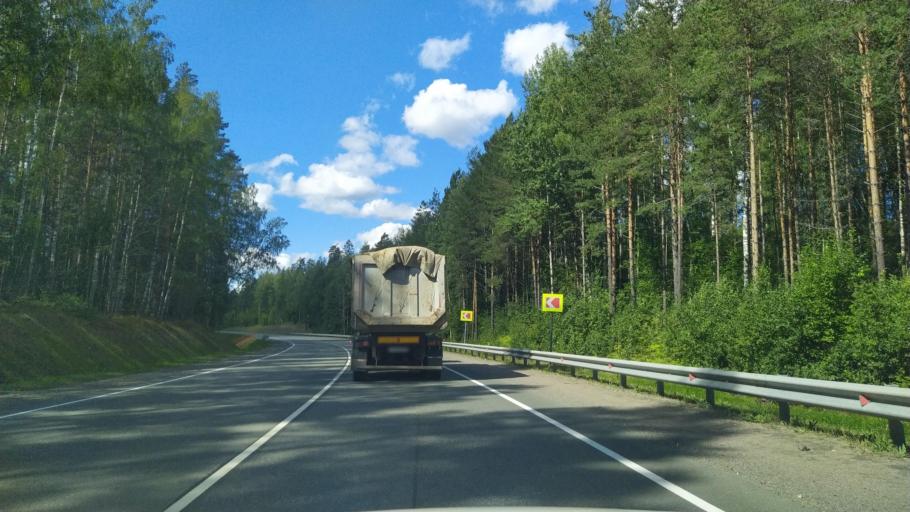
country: RU
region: Leningrad
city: Sapernoye
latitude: 60.7158
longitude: 30.0093
